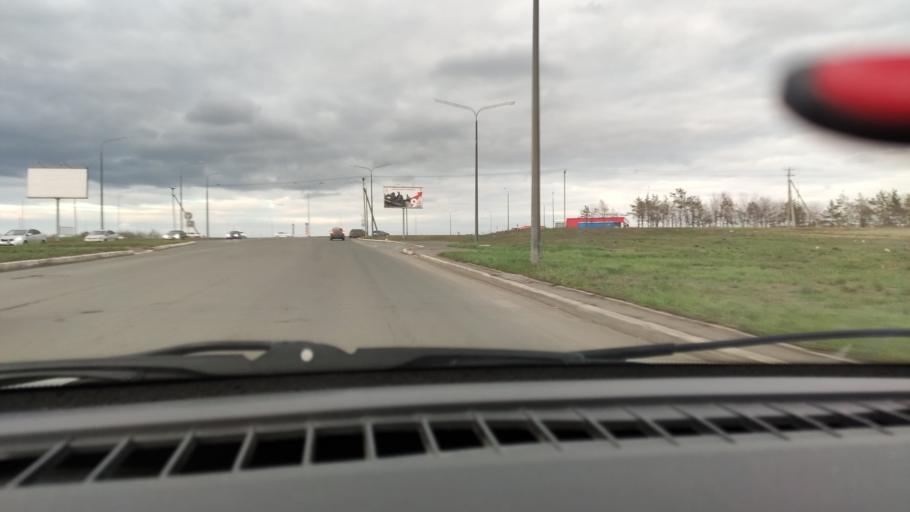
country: RU
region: Orenburg
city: Orenburg
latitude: 51.8109
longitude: 55.1823
